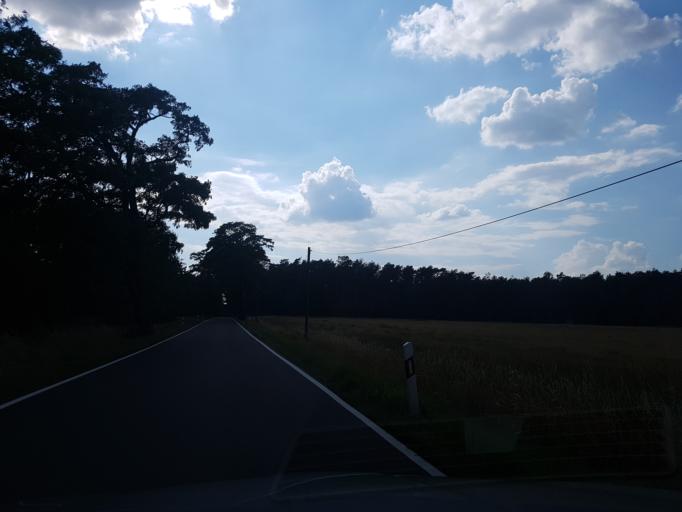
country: DE
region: Brandenburg
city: Schlieben
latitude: 51.6795
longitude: 13.3409
